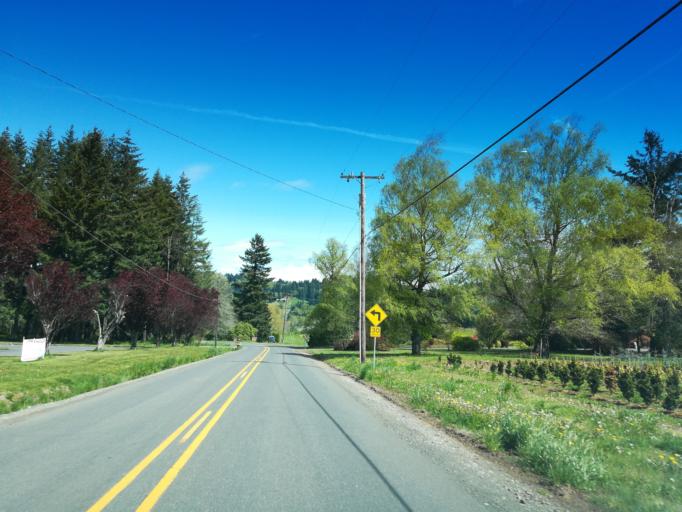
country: US
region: Oregon
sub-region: Clackamas County
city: Damascus
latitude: 45.4469
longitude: -122.4235
